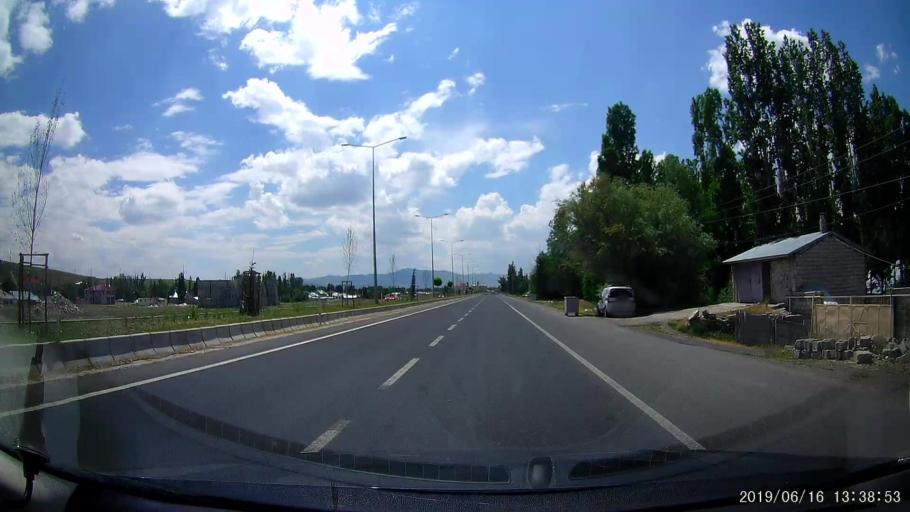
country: TR
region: Agri
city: Agri
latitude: 39.7099
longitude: 43.0672
